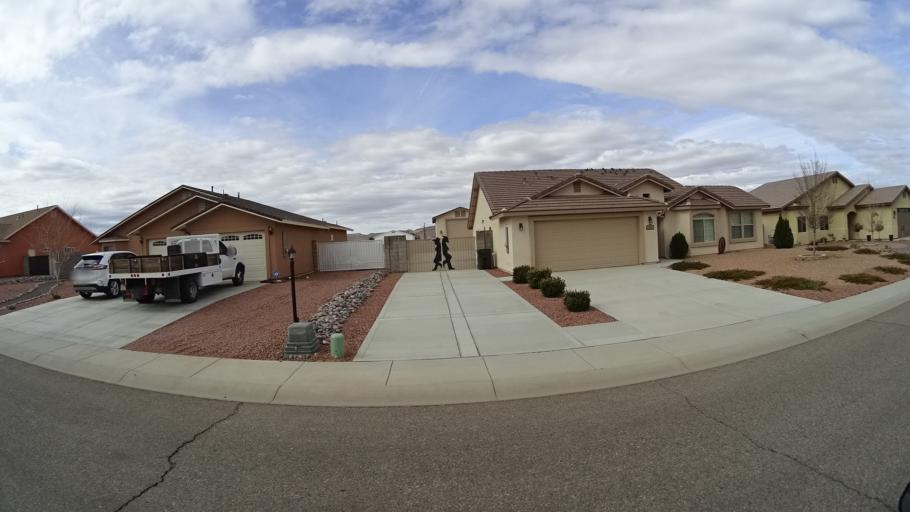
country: US
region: Arizona
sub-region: Mohave County
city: New Kingman-Butler
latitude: 35.2344
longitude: -114.0016
